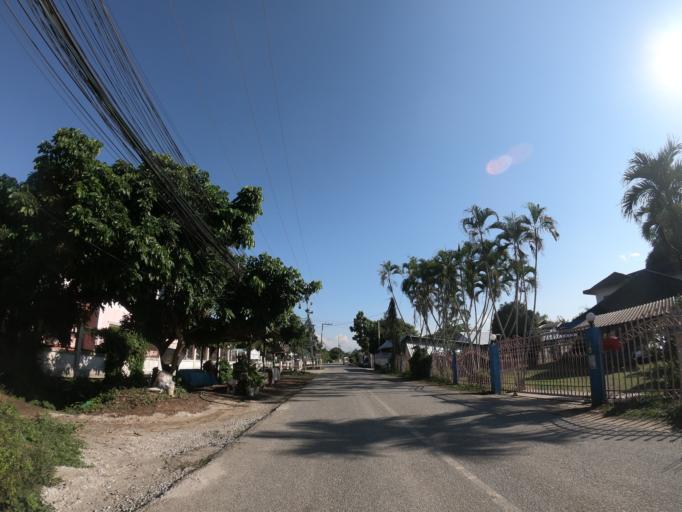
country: TH
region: Chiang Mai
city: Saraphi
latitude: 18.7056
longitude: 98.9863
